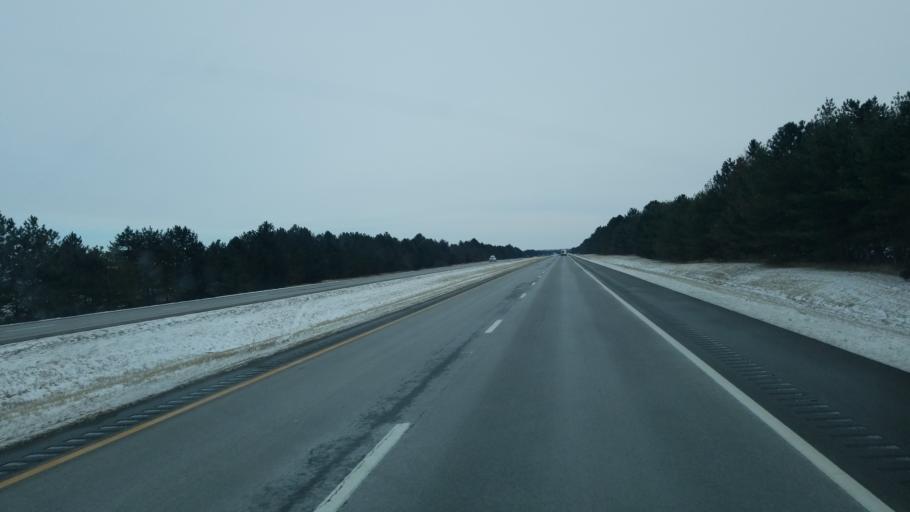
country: US
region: Ohio
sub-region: Wyandot County
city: Carey
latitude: 40.9558
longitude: -83.4434
